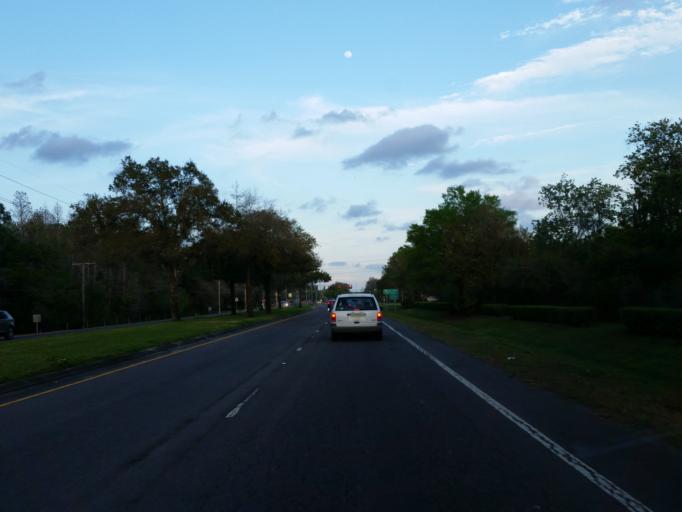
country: US
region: Florida
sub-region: Hillsborough County
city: Temple Terrace
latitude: 28.0691
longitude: -82.3719
